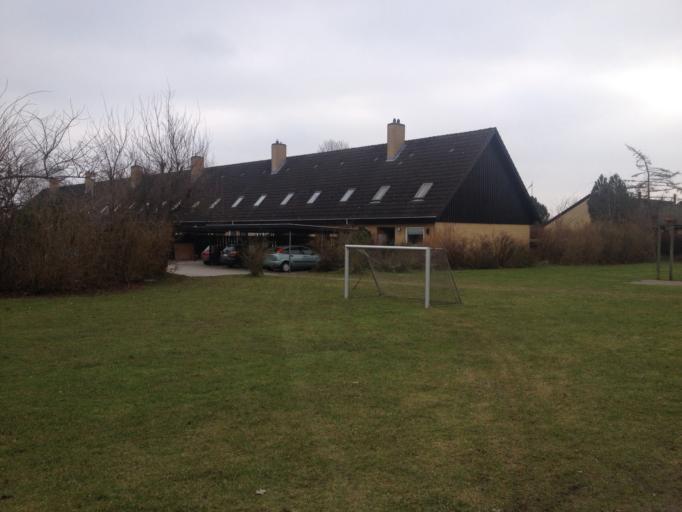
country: DK
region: Capital Region
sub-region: Egedal Kommune
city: Ganlose
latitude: 55.7929
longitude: 12.2685
